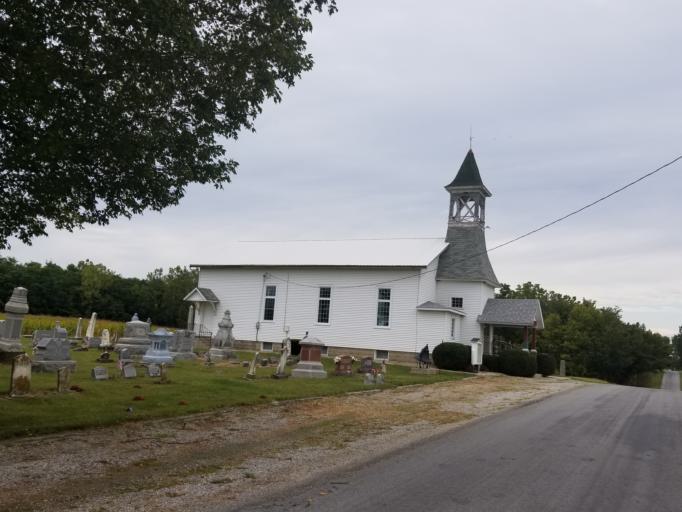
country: US
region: Ohio
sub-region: Wyandot County
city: Upper Sandusky
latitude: 40.8774
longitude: -83.1892
